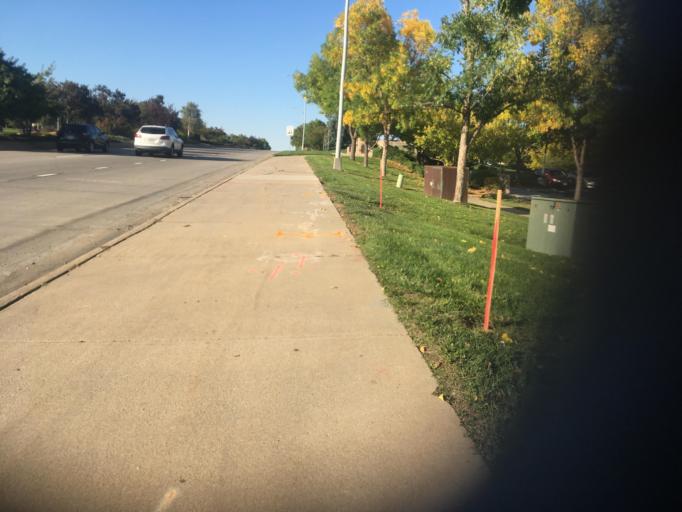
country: US
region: Colorado
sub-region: Broomfield County
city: Broomfield
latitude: 39.9303
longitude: -105.0903
